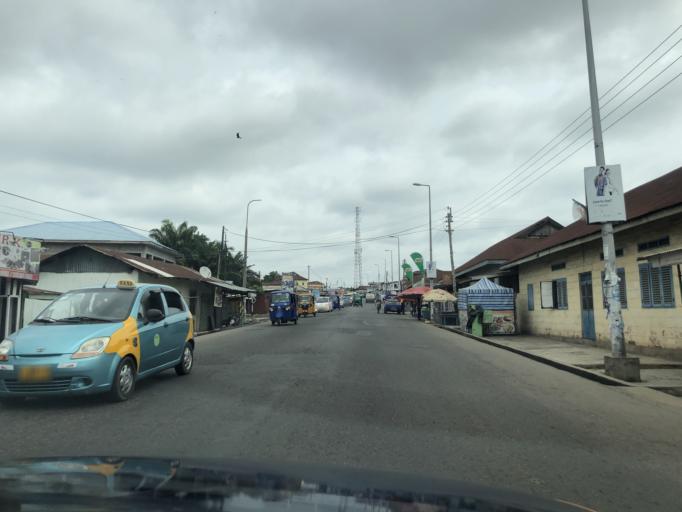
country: GH
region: Eastern
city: Koforidua
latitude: 6.0986
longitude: -0.2630
